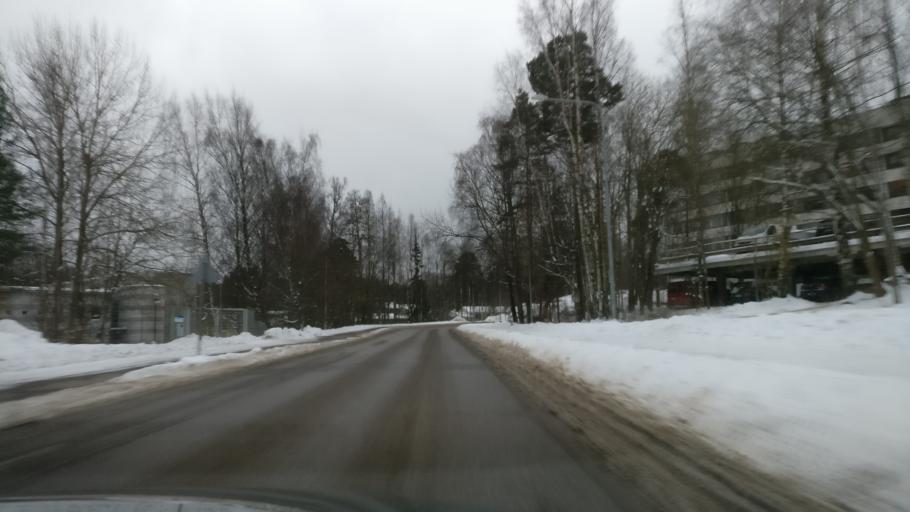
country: FI
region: Uusimaa
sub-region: Helsinki
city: Helsinki
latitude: 60.1768
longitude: 25.0482
